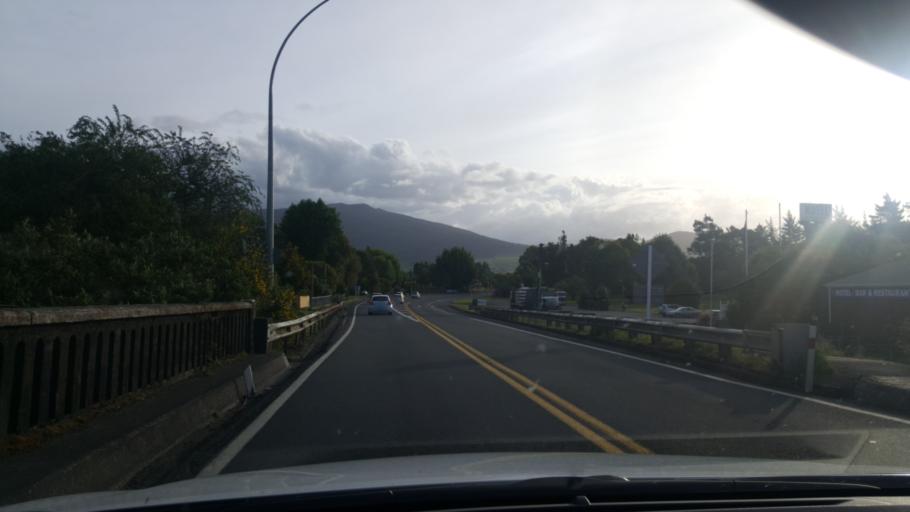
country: NZ
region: Waikato
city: Turangi
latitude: -38.9863
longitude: 175.8188
